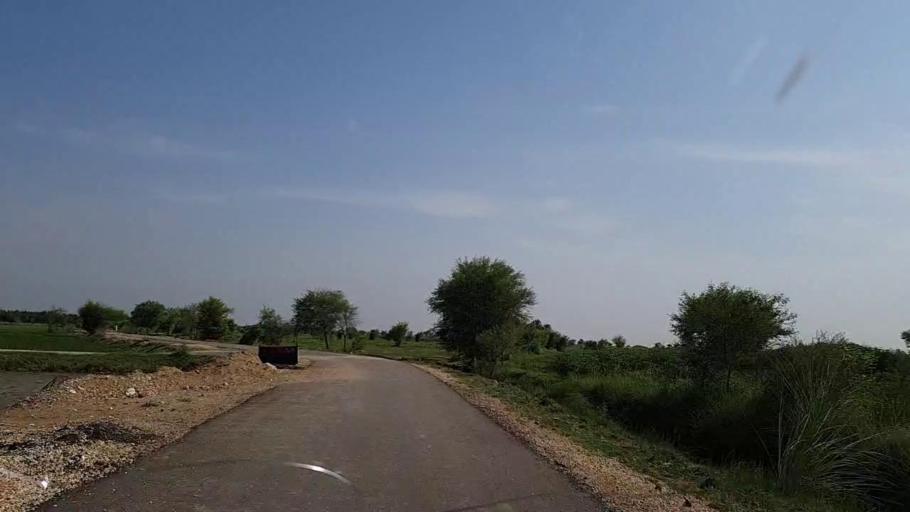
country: PK
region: Sindh
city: Khanpur
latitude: 27.6988
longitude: 69.3642
